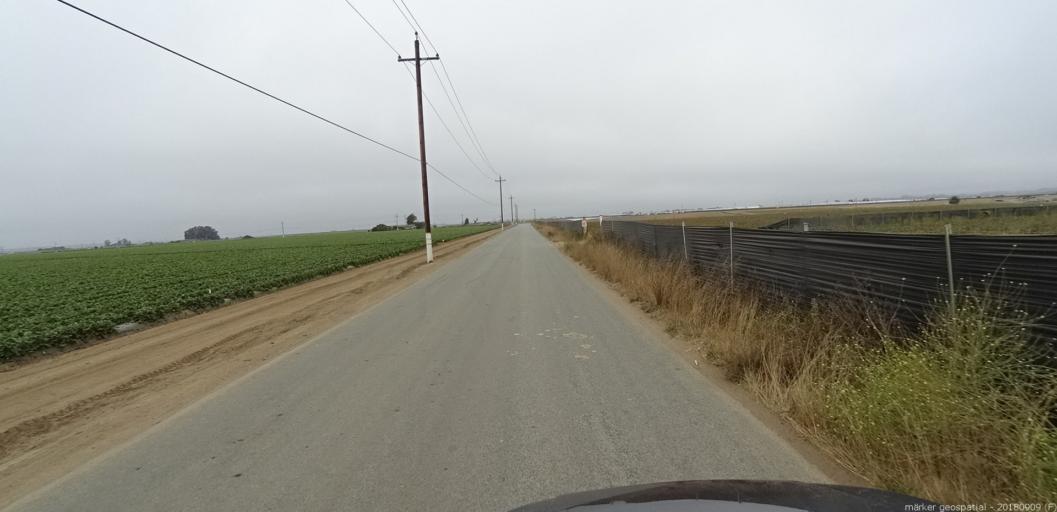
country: US
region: California
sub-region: Monterey County
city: Boronda
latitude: 36.7249
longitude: -121.6690
